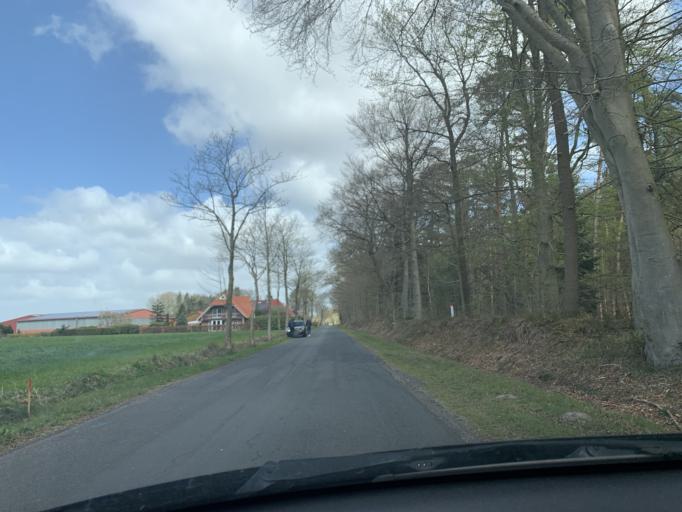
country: DE
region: Lower Saxony
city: Westerstede
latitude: 53.2762
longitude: 7.9405
